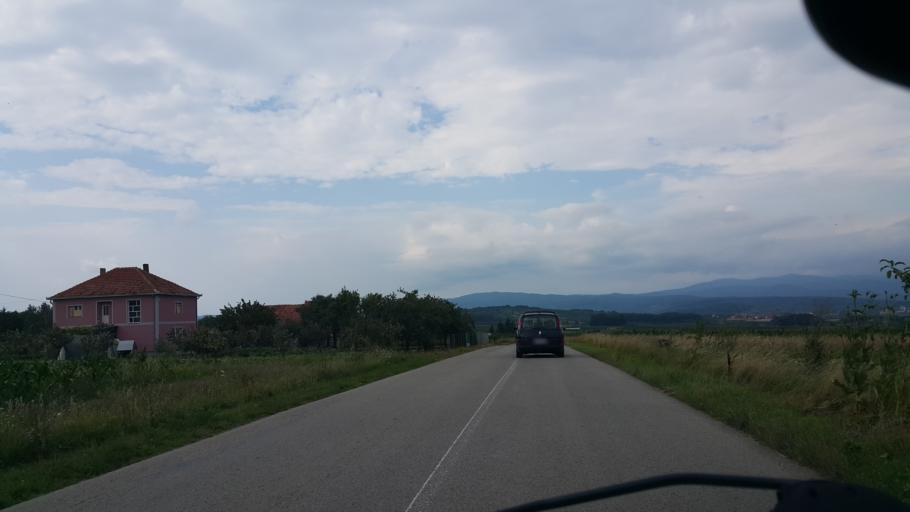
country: RS
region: Central Serbia
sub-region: Toplicki Okrug
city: Blace
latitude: 43.2661
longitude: 21.2732
